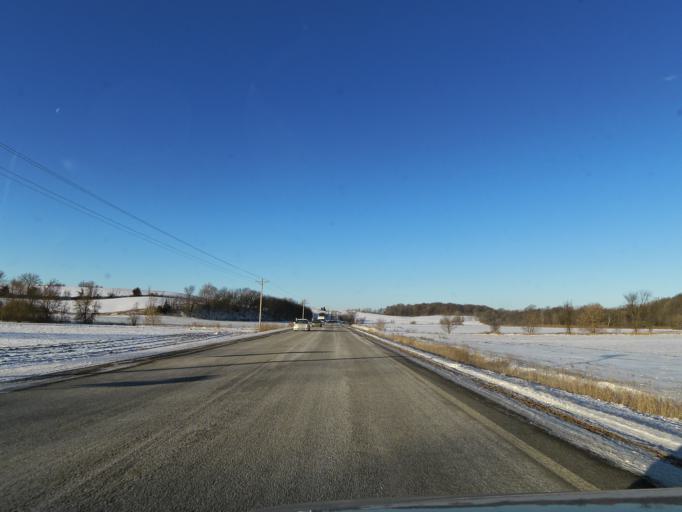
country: US
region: Minnesota
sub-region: Scott County
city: Jordan
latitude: 44.6305
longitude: -93.5404
